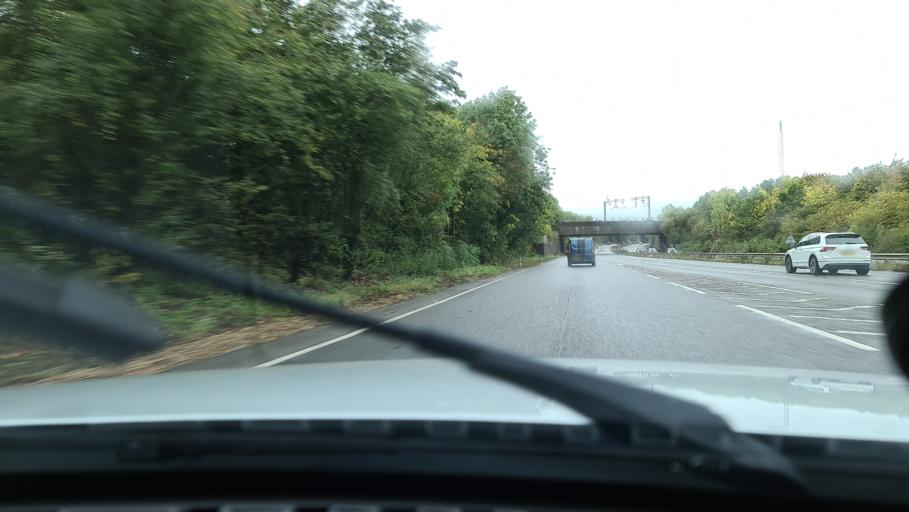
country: GB
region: England
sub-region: Buckinghamshire
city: Bletchley
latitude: 52.0119
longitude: -0.7435
